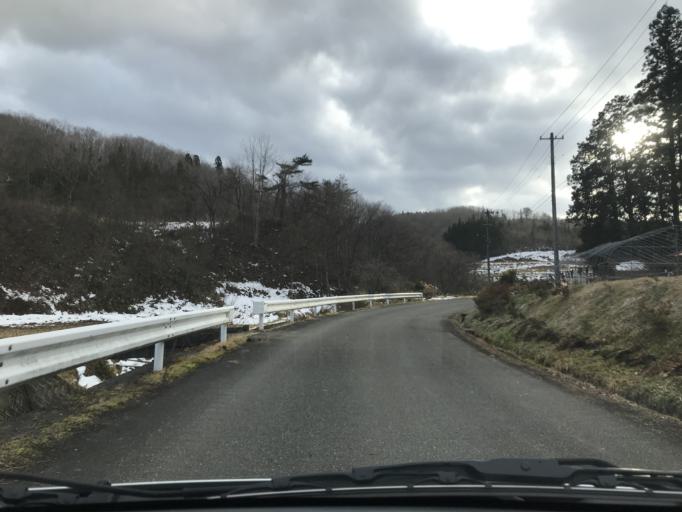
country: JP
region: Iwate
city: Ichinoseki
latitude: 38.9987
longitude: 141.0031
